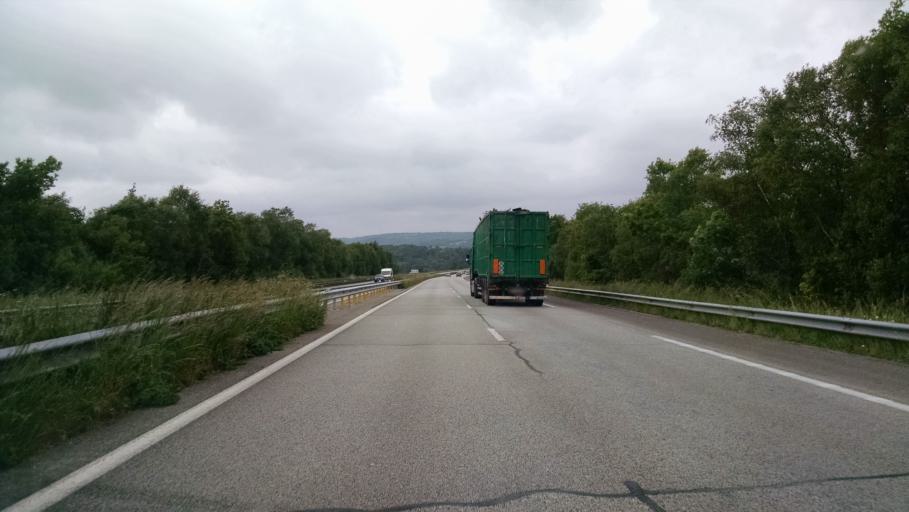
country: FR
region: Brittany
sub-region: Departement du Finistere
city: Chateaulin
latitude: 48.2309
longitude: -4.0962
